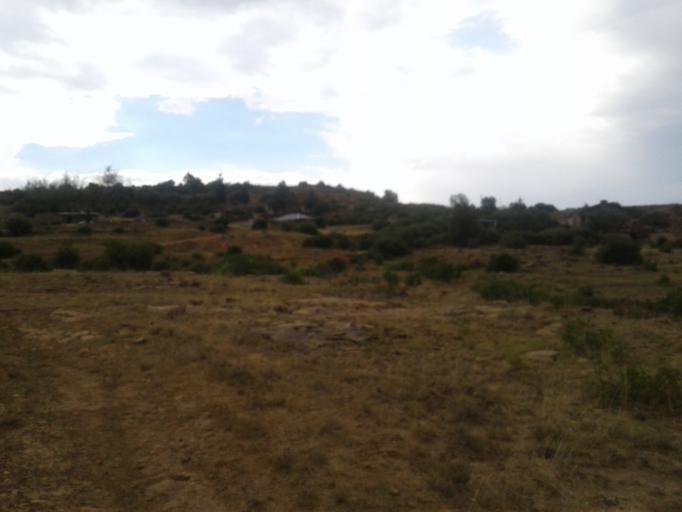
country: LS
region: Quthing
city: Quthing
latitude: -30.3841
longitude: 27.5613
